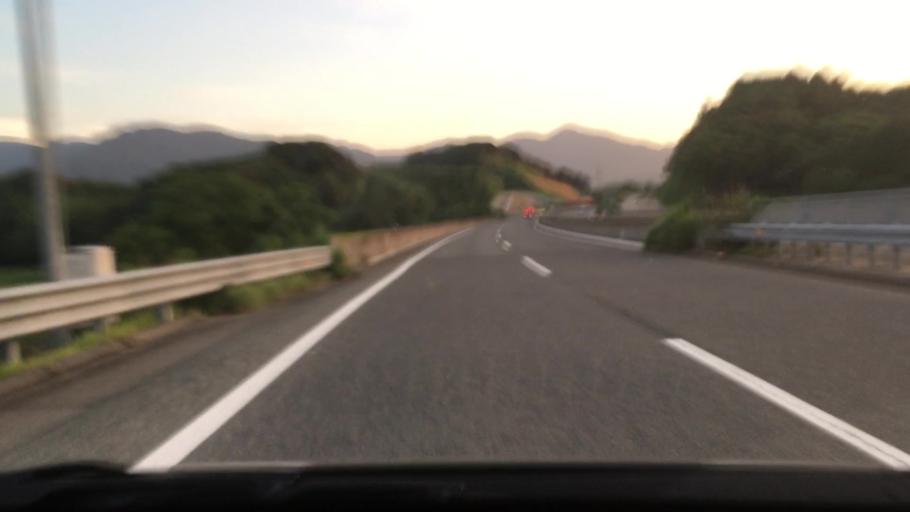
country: JP
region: Fukuoka
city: Maebaru-chuo
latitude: 33.5349
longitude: 130.1938
